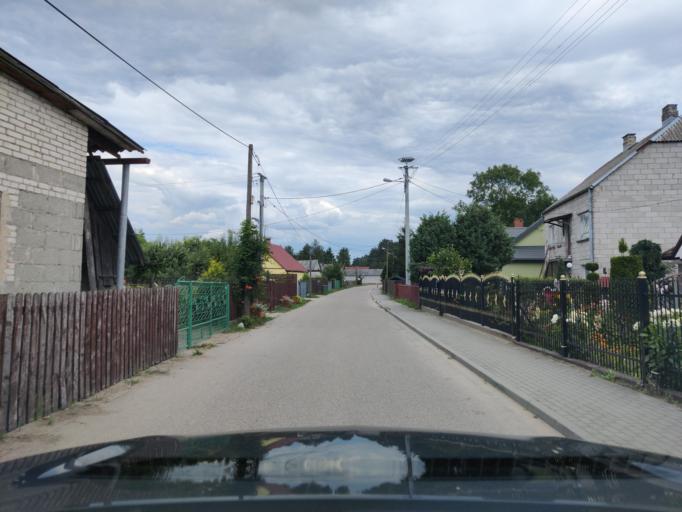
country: PL
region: Masovian Voivodeship
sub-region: Powiat pultuski
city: Pultusk
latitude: 52.7264
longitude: 21.1215
